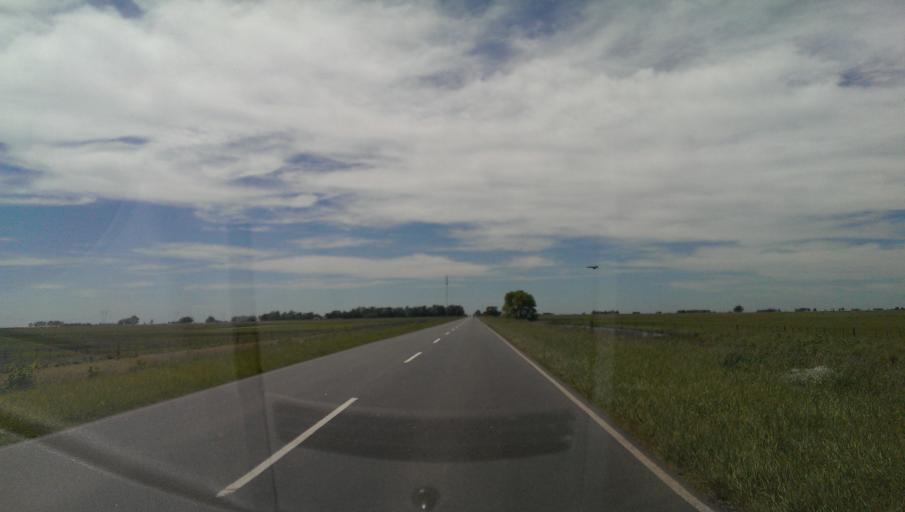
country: AR
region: Buenos Aires
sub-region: Partido de Laprida
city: Laprida
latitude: -37.1995
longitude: -60.6692
